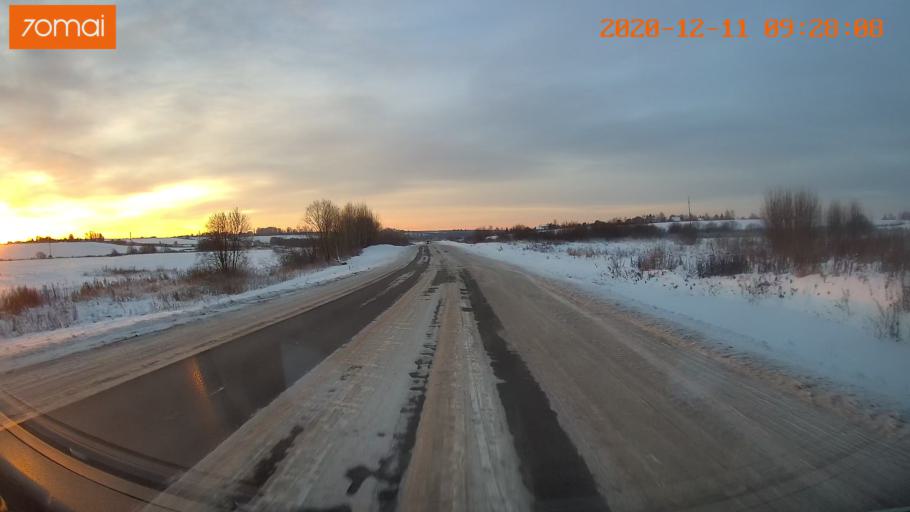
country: RU
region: Vologda
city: Vologda
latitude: 59.1567
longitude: 40.0099
